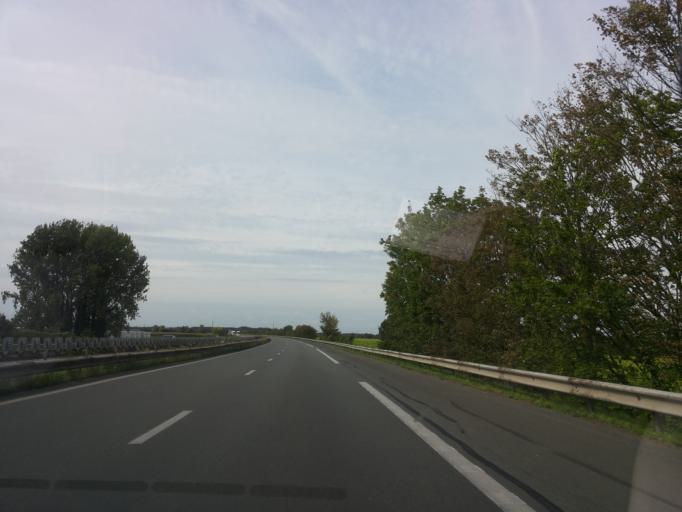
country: FR
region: Nord-Pas-de-Calais
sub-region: Departement du Pas-de-Calais
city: Allouagne
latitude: 50.5423
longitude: 2.5295
